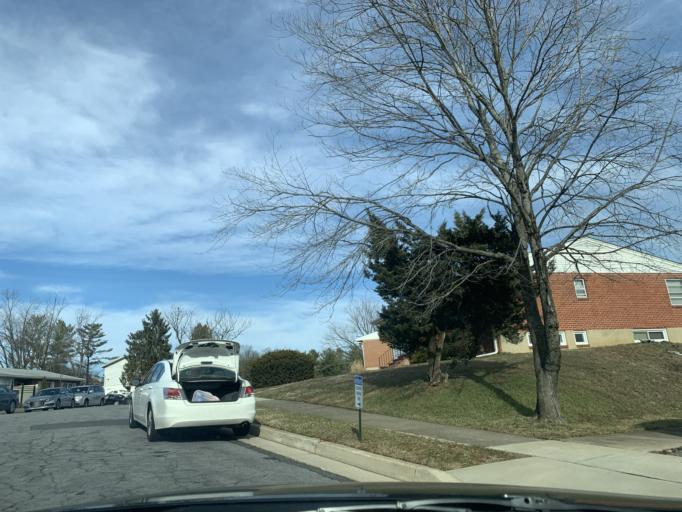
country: US
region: Maryland
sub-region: Baltimore County
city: Pikesville
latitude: 39.3682
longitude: -76.7459
